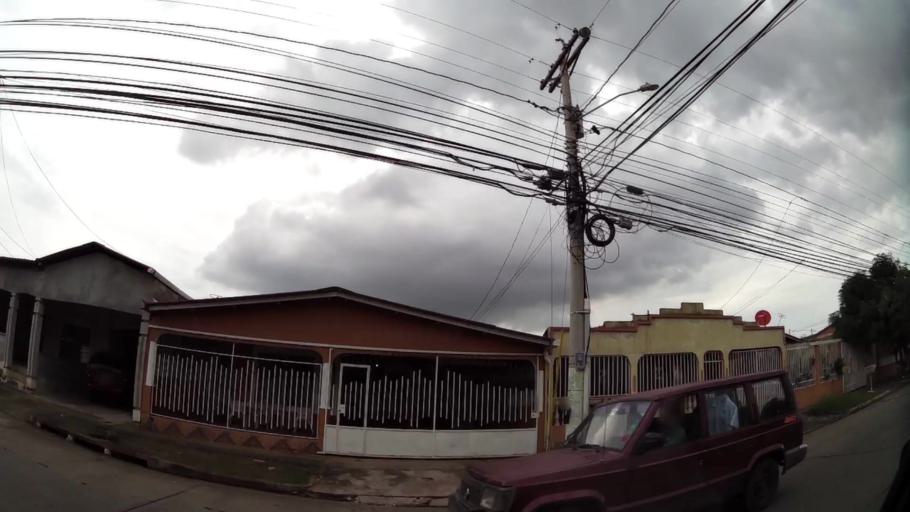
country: PA
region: Panama
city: Tocumen
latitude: 9.0486
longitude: -79.4074
